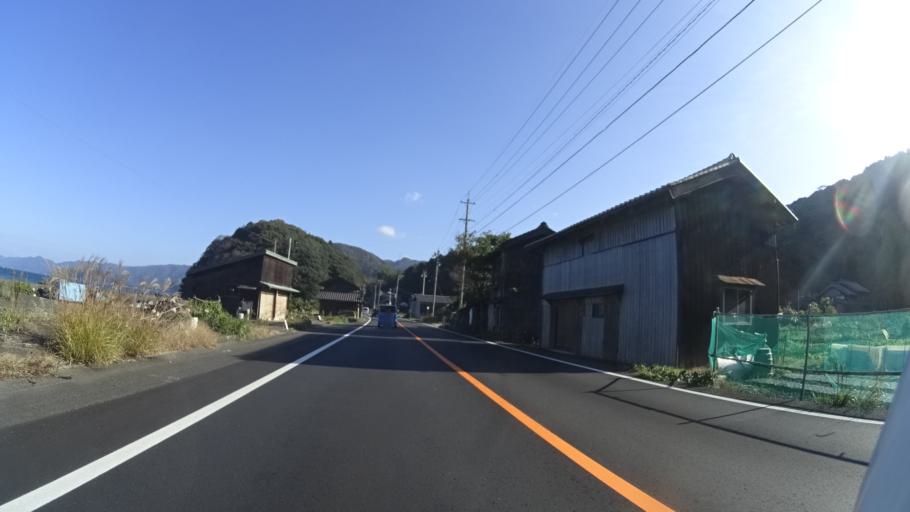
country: JP
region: Fukui
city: Tsuruga
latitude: 35.7043
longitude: 136.0825
